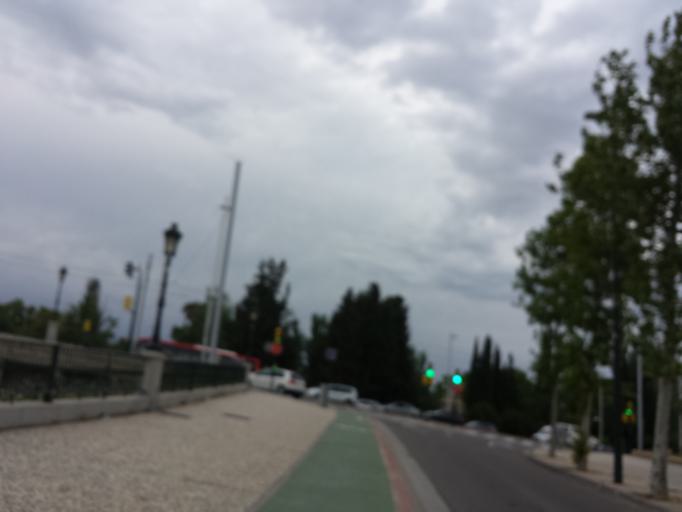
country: ES
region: Aragon
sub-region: Provincia de Zaragoza
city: Delicias
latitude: 41.6278
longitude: -0.9077
